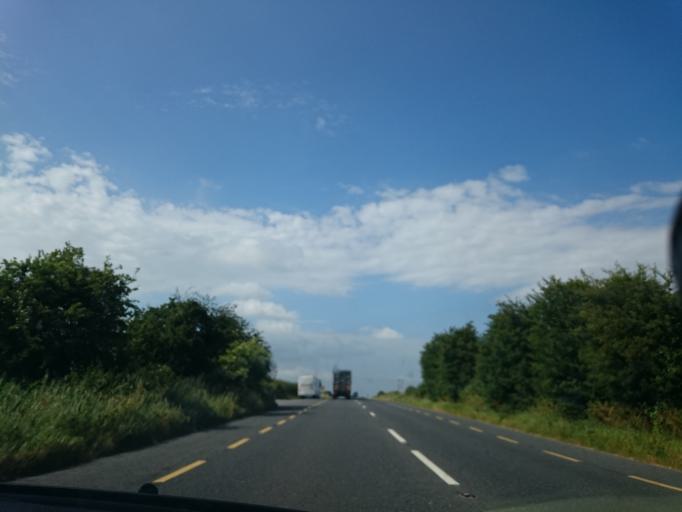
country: IE
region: Leinster
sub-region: Kilkenny
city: Kilkenny
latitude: 52.6004
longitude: -7.2420
